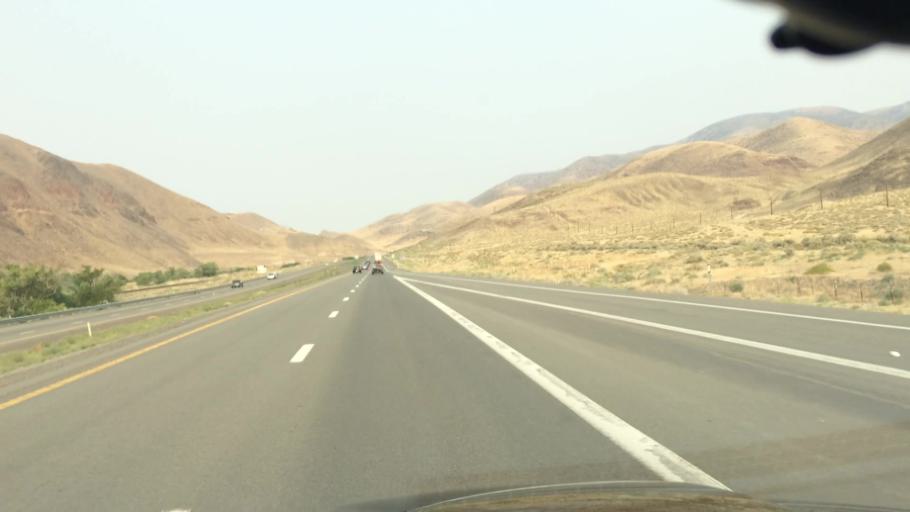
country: US
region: Nevada
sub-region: Lyon County
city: Fernley
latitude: 39.5895
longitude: -119.4315
